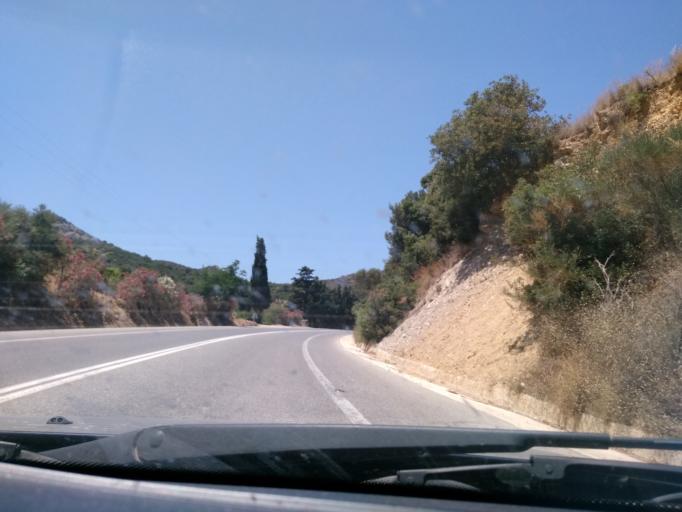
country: GR
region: Crete
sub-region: Nomos Rethymnis
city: Anogeia
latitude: 35.4006
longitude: 24.8697
